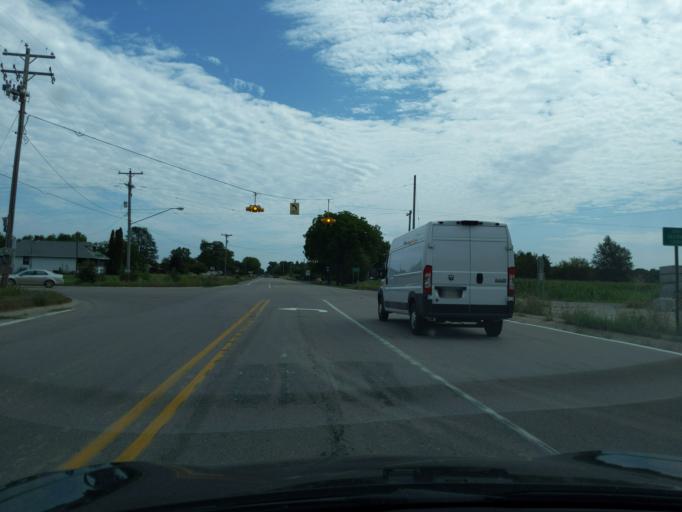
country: US
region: Michigan
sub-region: Gratiot County
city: Breckenridge
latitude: 43.4081
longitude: -84.3705
